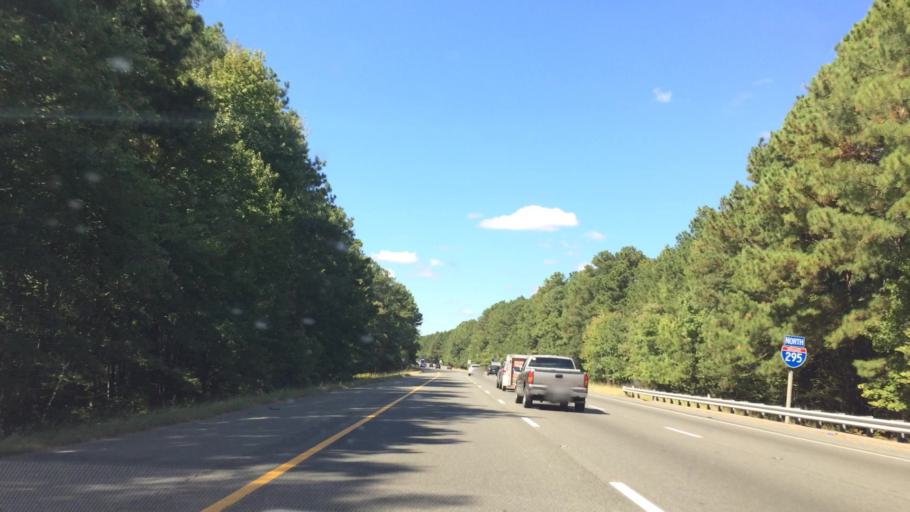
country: US
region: Virginia
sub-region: Henrico County
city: Glen Allen
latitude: 37.6723
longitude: -77.4928
